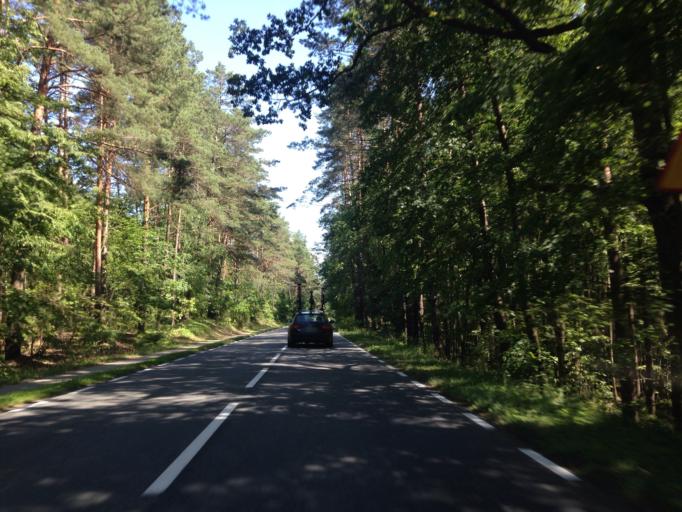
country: PL
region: Kujawsko-Pomorskie
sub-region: Powiat swiecki
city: Osie
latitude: 53.6123
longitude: 18.2932
